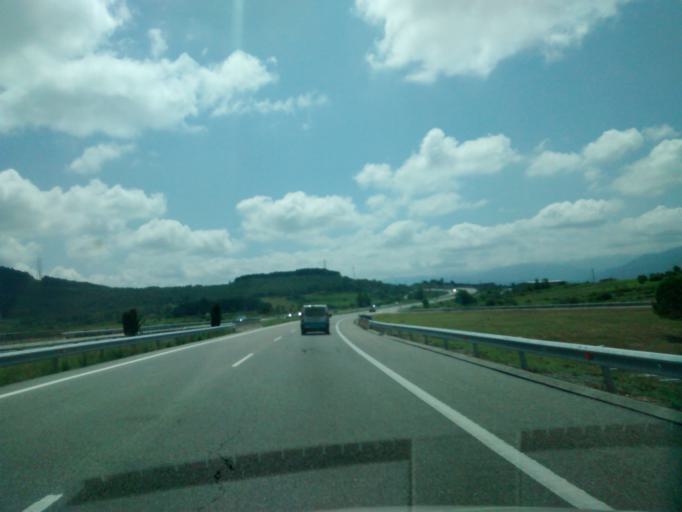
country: ES
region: Castille and Leon
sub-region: Provincia de Leon
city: Ponferrada
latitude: 42.5802
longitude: -6.6056
